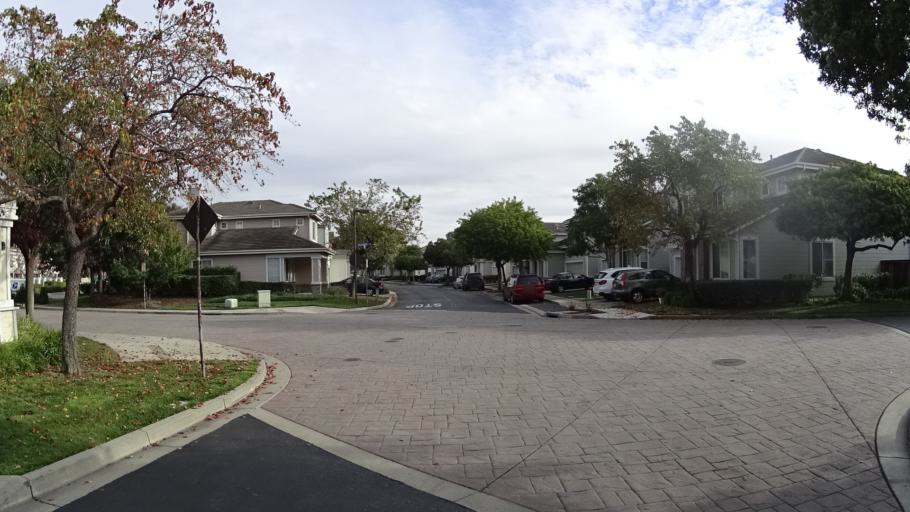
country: US
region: California
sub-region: San Mateo County
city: Redwood Shores
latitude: 37.5402
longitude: -122.2373
